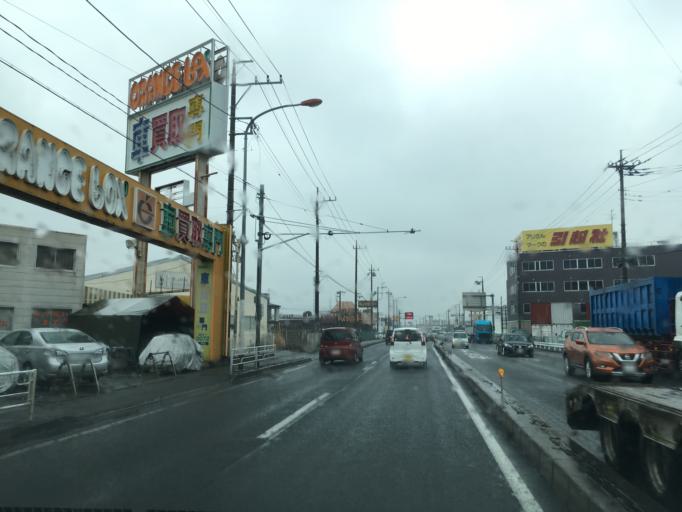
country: JP
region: Saitama
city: Koshigaya
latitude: 35.8723
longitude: 139.7784
